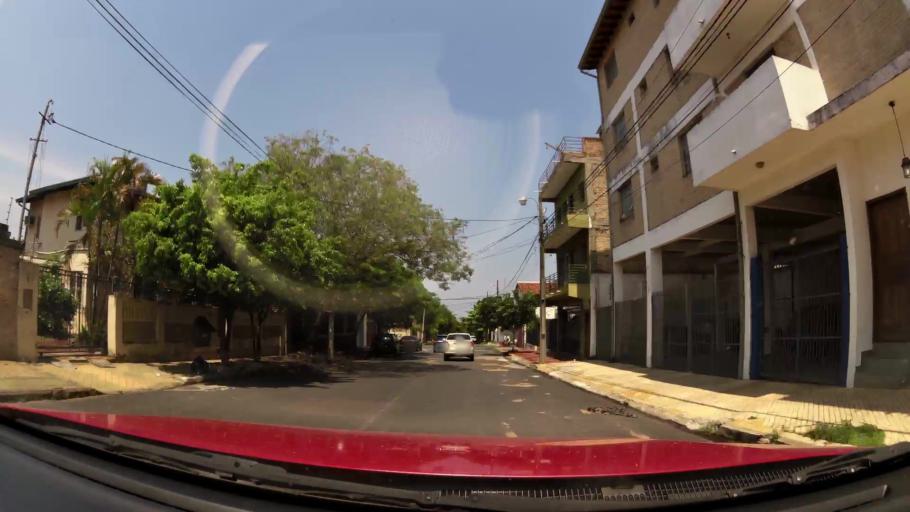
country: PY
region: Asuncion
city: Asuncion
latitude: -25.3019
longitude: -57.6477
